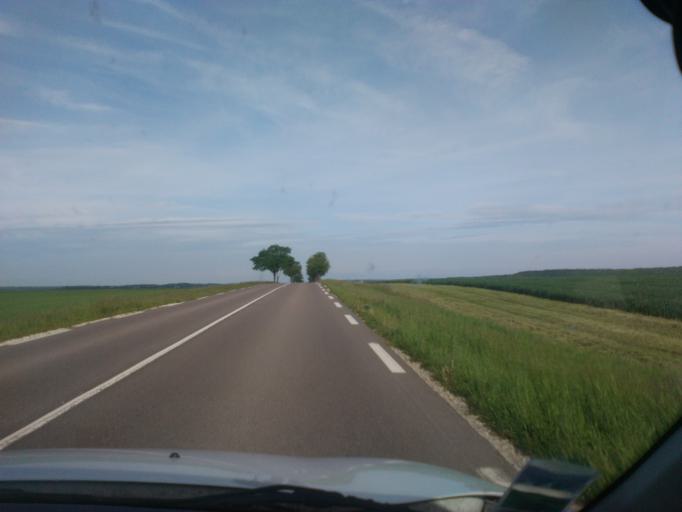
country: FR
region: Champagne-Ardenne
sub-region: Departement de l'Aube
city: Vendeuvre-sur-Barse
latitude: 48.2357
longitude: 4.5127
